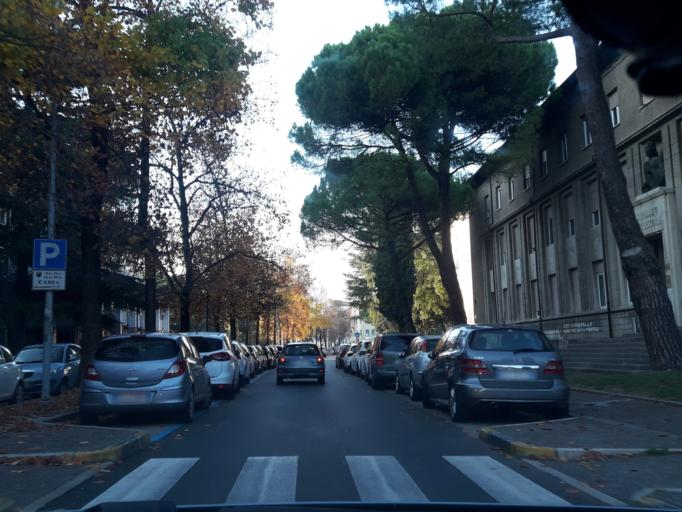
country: IT
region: Friuli Venezia Giulia
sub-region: Provincia di Udine
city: Udine
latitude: 46.0611
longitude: 13.2427
